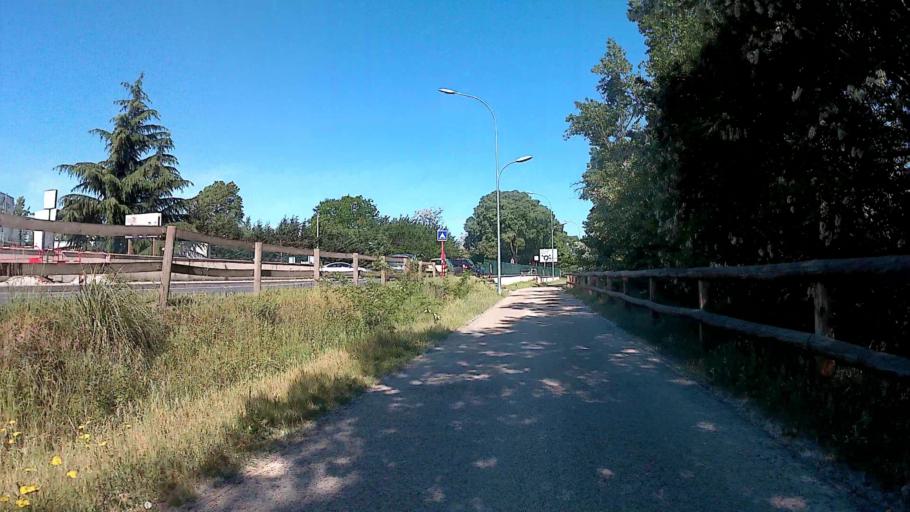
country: FR
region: Aquitaine
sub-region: Departement de la Gironde
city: Villenave-d'Ornon
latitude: 44.7804
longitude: -0.5350
